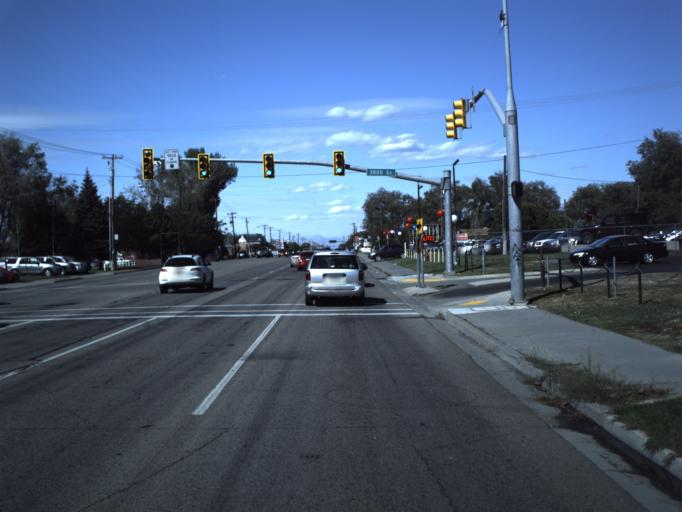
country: US
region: Utah
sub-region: Salt Lake County
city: Taylorsville
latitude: 40.6890
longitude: -111.9388
